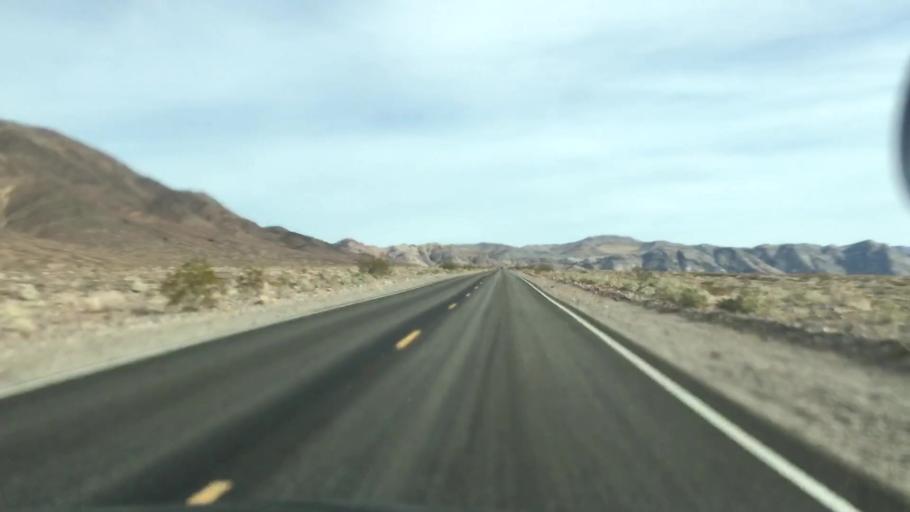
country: US
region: Nevada
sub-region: Nye County
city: Beatty
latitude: 36.7044
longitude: -116.9946
